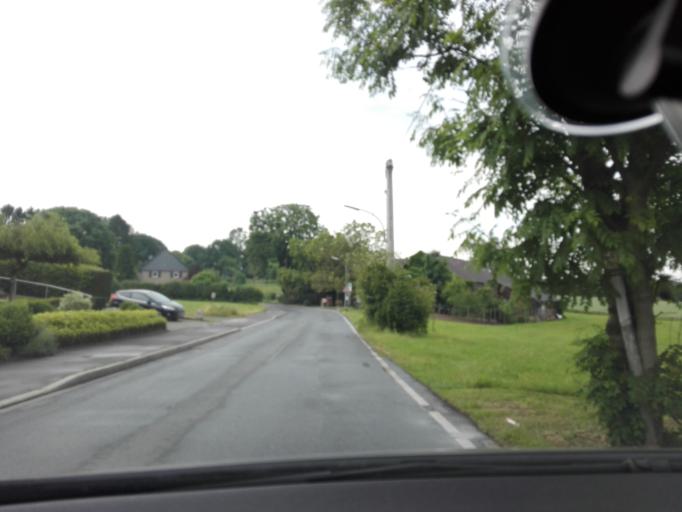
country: DE
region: North Rhine-Westphalia
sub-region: Regierungsbezirk Arnsberg
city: Unna
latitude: 51.5218
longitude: 7.7221
